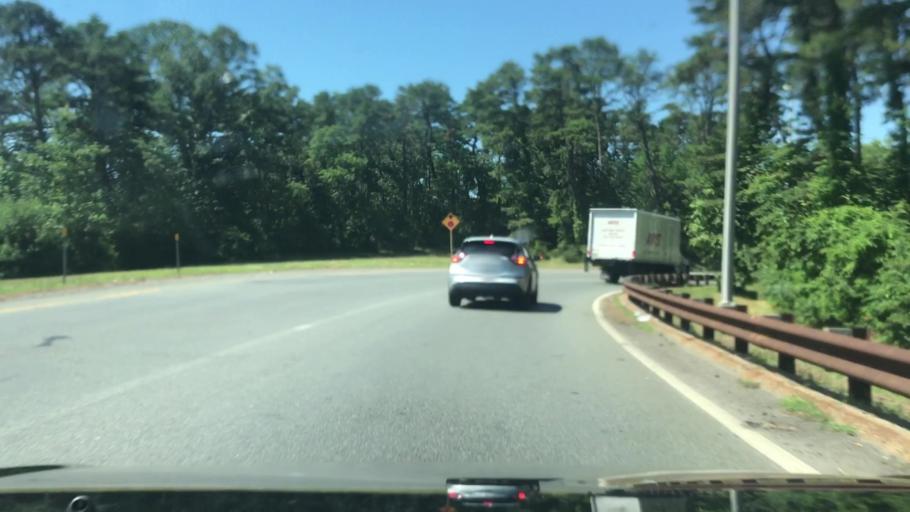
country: US
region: New Jersey
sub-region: Ocean County
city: South Toms River
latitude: 39.9413
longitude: -74.2094
